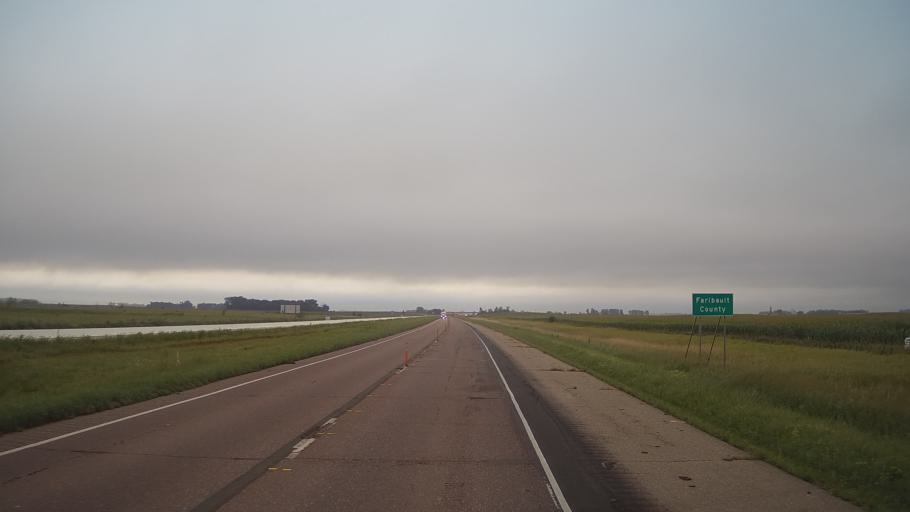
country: US
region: Minnesota
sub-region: Faribault County
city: Winnebago
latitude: 43.6660
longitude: -94.2482
